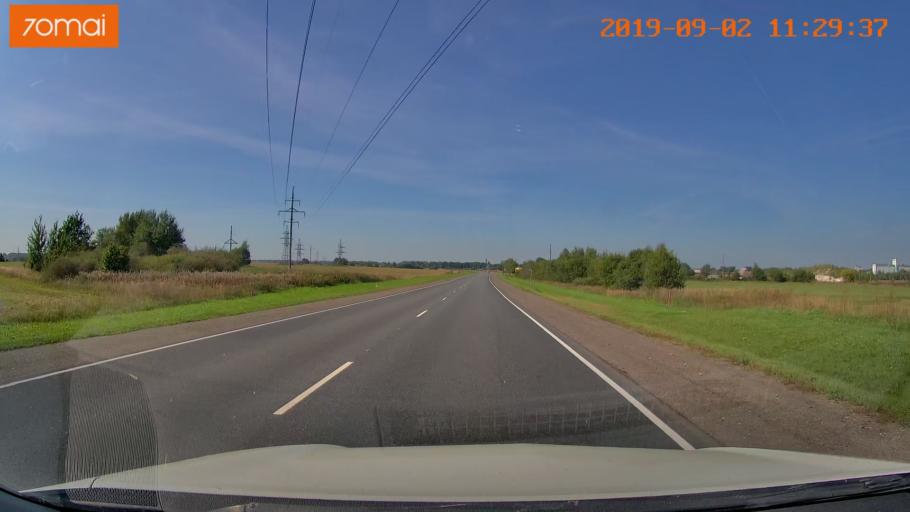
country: RU
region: Smolensk
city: Roslavl'
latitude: 53.9886
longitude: 32.8558
